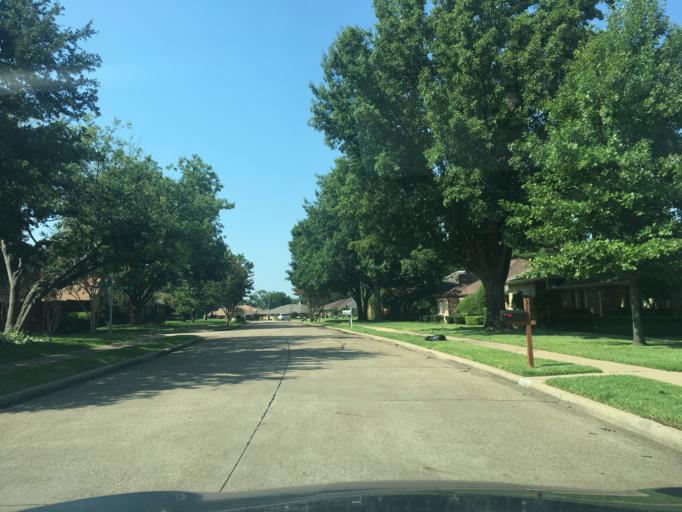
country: US
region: Texas
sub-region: Dallas County
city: Garland
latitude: 32.9479
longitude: -96.6340
